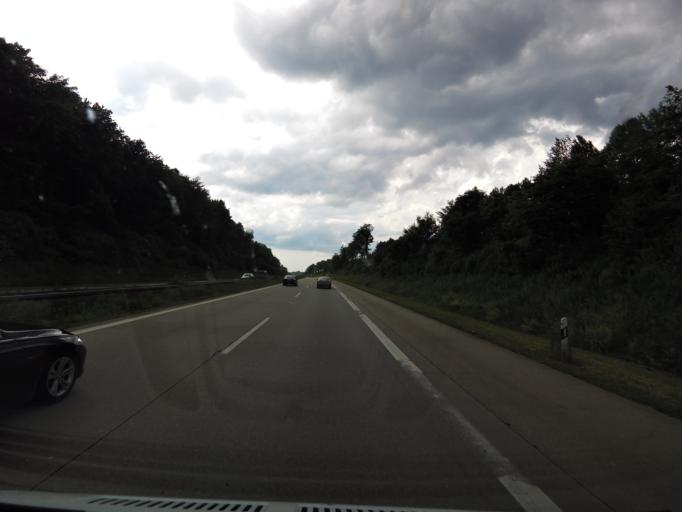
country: DE
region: Bavaria
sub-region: Lower Bavaria
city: Iggensbach
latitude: 48.7383
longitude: 13.1203
